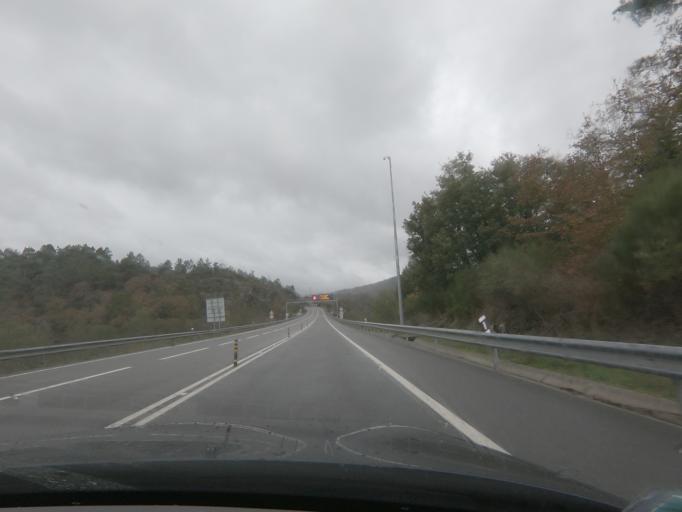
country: PT
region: Vila Real
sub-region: Santa Marta de Penaguiao
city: Santa Marta de Penaguiao
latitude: 41.2841
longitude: -7.8260
